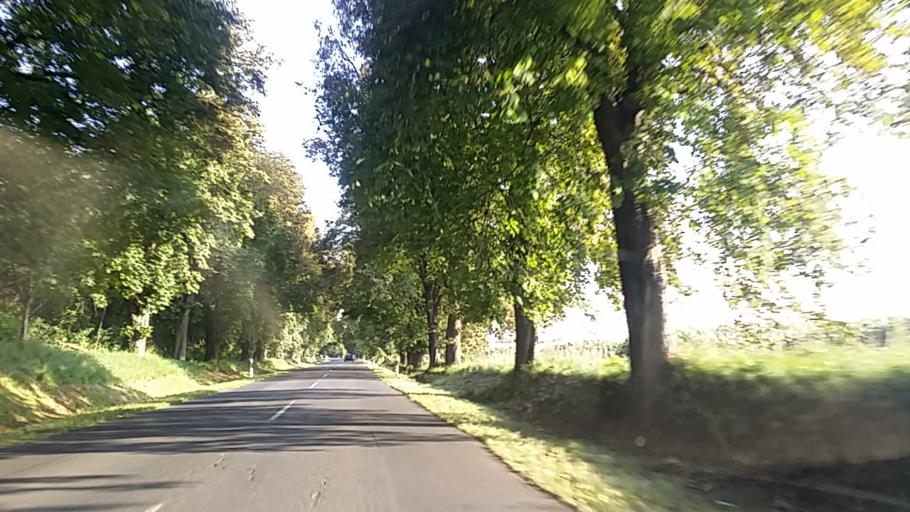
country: HU
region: Zala
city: Keszthely
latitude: 46.7299
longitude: 17.2403
